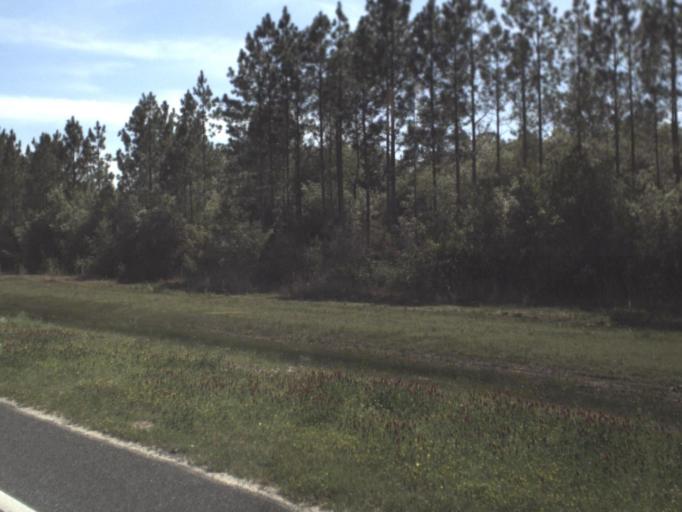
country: US
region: Florida
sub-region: Bay County
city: Lynn Haven
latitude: 30.3483
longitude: -85.6638
